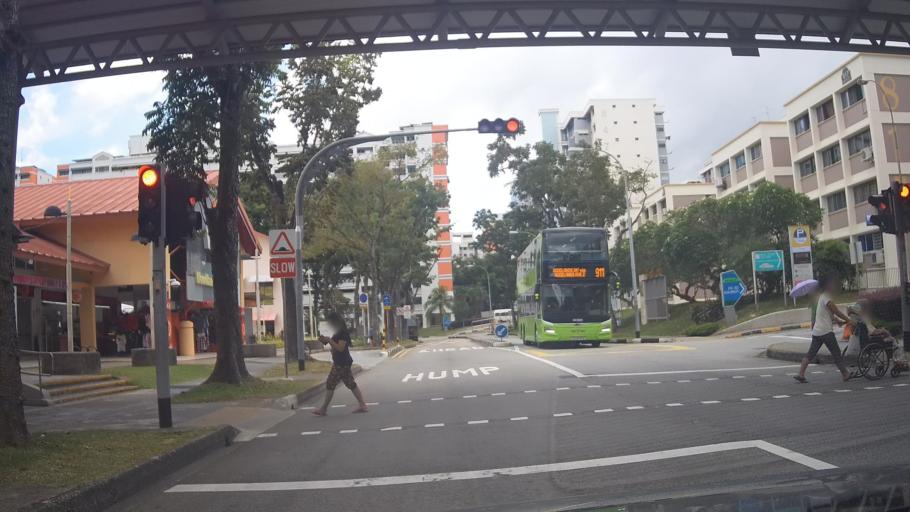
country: MY
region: Johor
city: Johor Bahru
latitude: 1.4423
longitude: 103.7907
